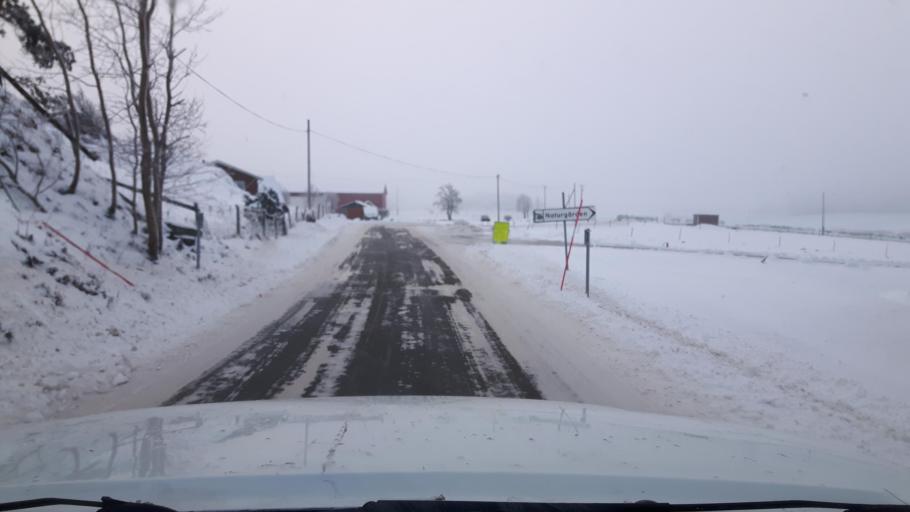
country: SE
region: Halland
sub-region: Kungsbacka Kommun
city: Vallda
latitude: 57.4738
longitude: 12.0281
